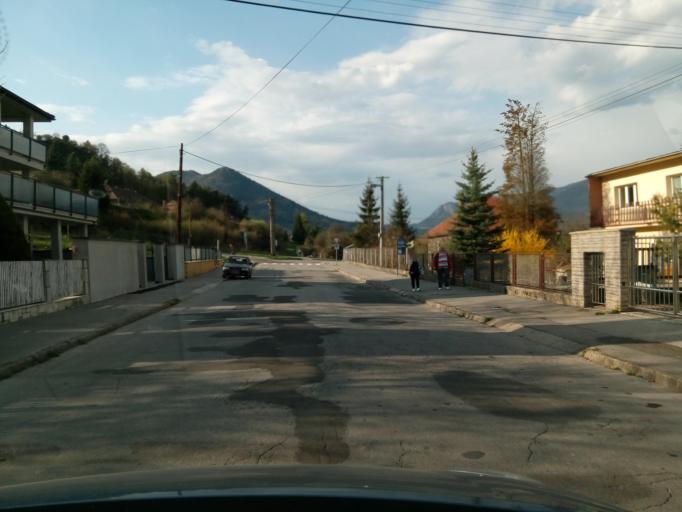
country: SK
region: Zilinsky
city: Ruzomberok
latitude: 49.0682
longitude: 19.2977
